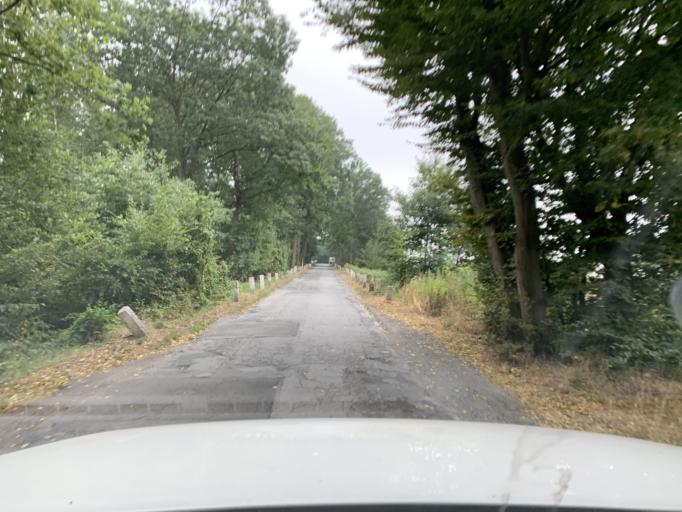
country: DE
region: North Rhine-Westphalia
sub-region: Regierungsbezirk Dusseldorf
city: Hochfeld
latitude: 51.3799
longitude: 6.8137
